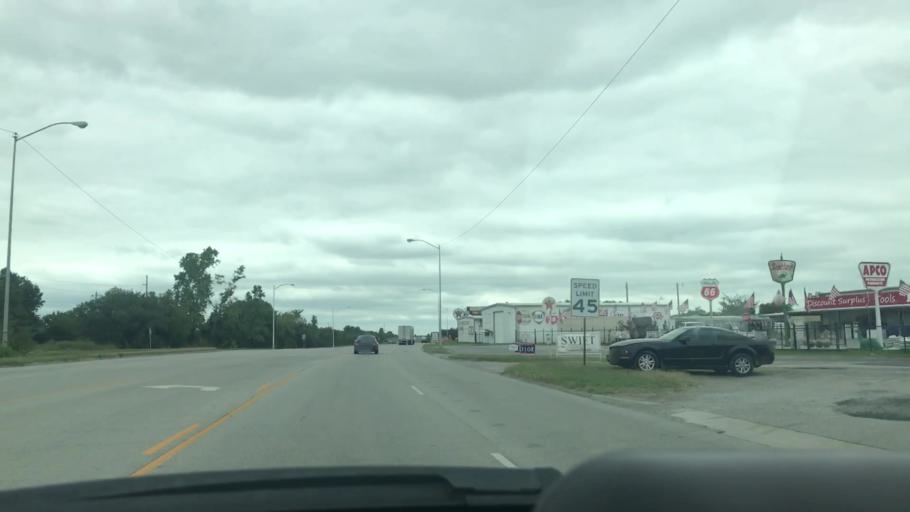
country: US
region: Oklahoma
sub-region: Mayes County
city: Pryor
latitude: 36.3156
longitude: -95.3159
